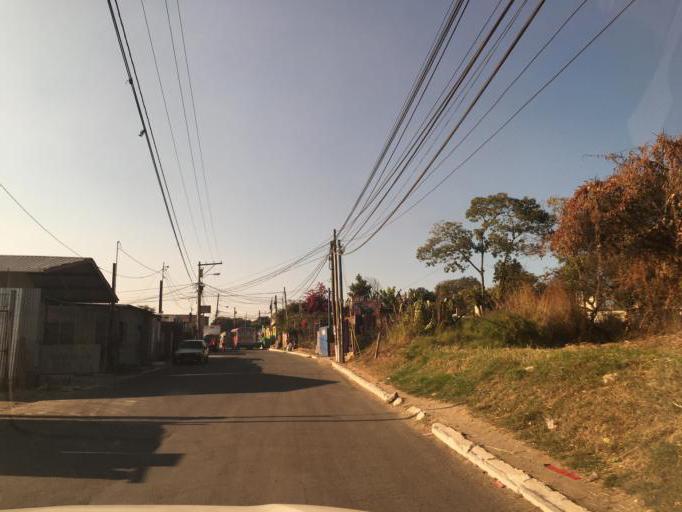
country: GT
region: Guatemala
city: Mixco
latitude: 14.6148
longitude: -90.5779
